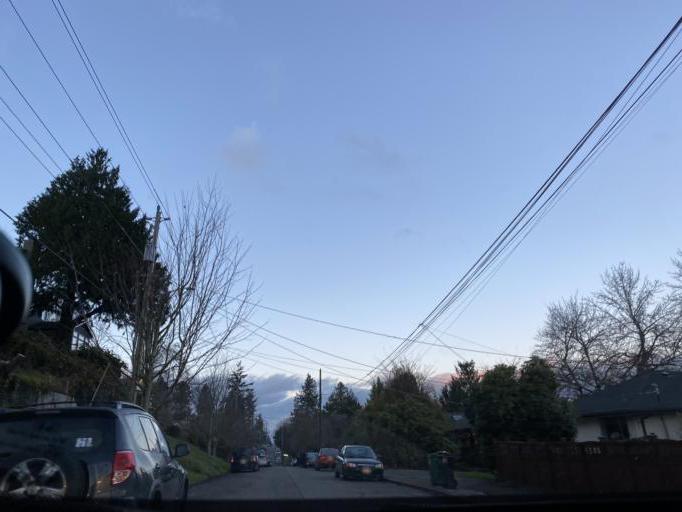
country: US
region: Washington
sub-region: King County
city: Seattle
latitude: 47.6454
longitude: -122.3859
